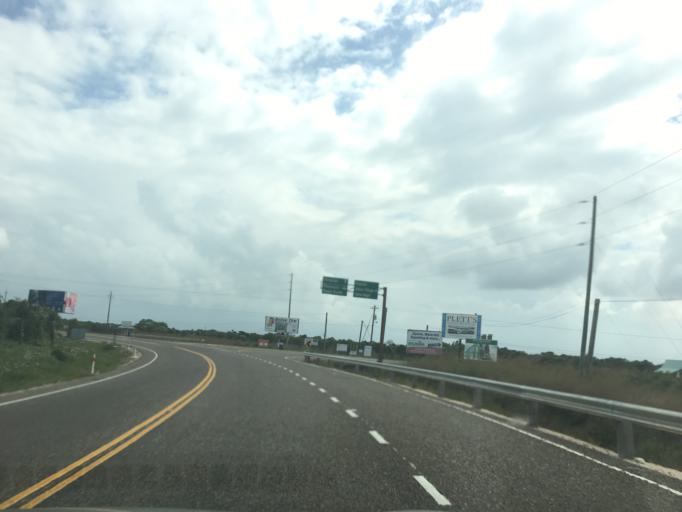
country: BZ
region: Stann Creek
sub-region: Dangriga
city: Dangriga
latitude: 16.9813
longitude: -88.2955
